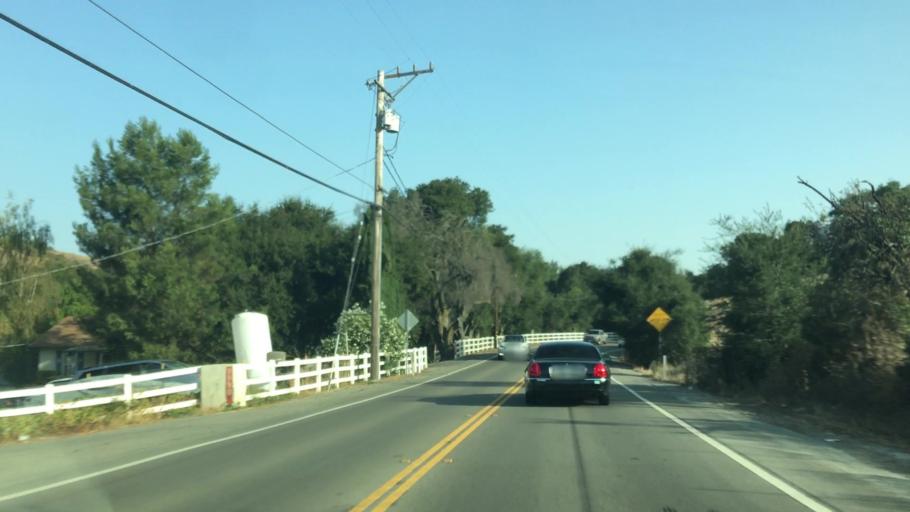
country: US
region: California
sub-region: Contra Costa County
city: San Ramon
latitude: 37.7488
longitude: -122.0313
